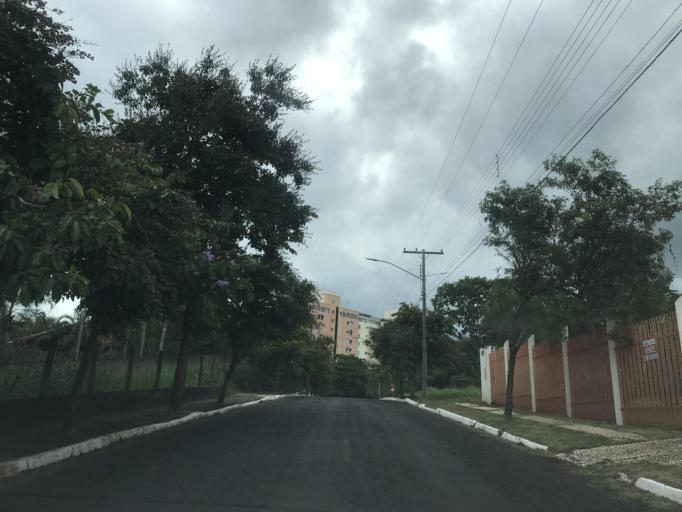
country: BR
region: Goias
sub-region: Caldas Novas
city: Caldas Novas
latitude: -17.7690
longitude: -48.7576
